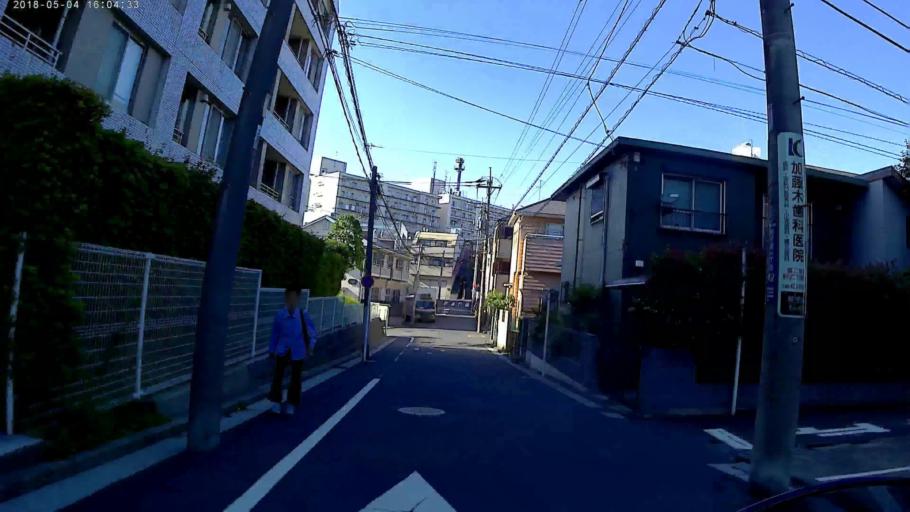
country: JP
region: Kanagawa
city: Yokohama
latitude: 35.4912
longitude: 139.6566
